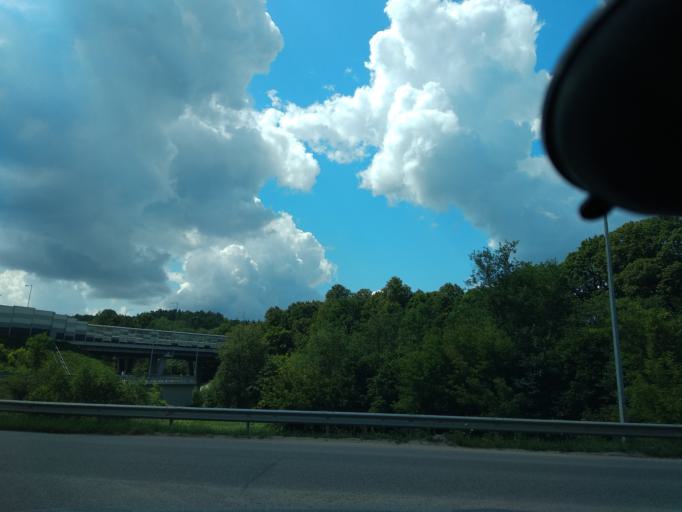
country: LT
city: Grigiskes
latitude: 54.6787
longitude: 25.0766
